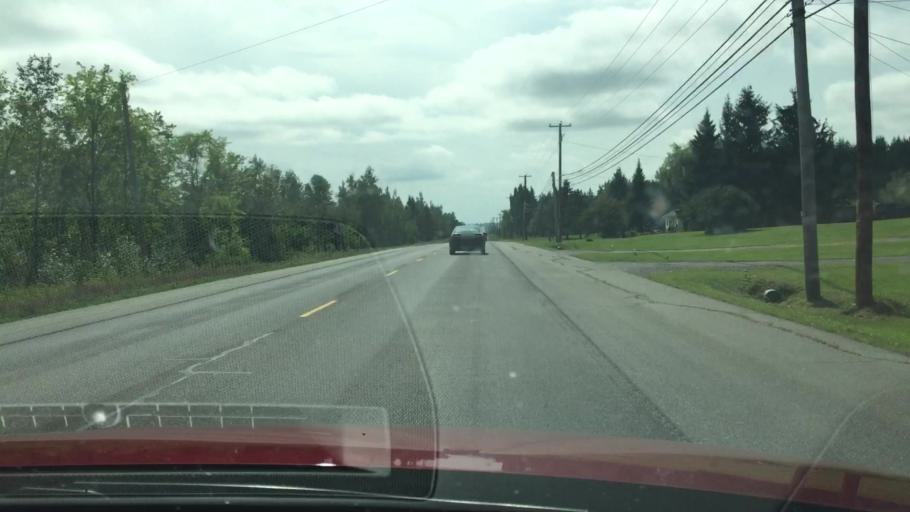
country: US
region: Maine
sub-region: Aroostook County
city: Houlton
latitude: 46.3337
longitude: -67.8418
